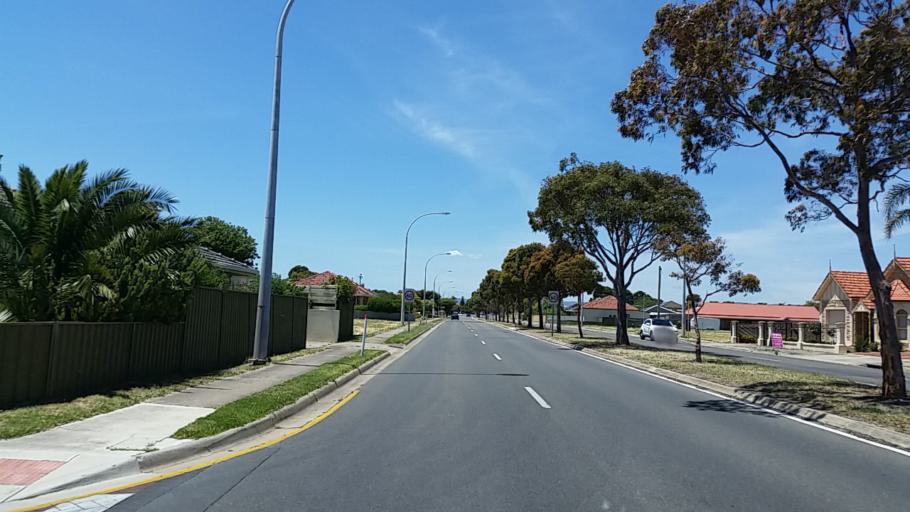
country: AU
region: South Australia
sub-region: Charles Sturt
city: Grange
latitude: -34.8921
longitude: 138.4998
